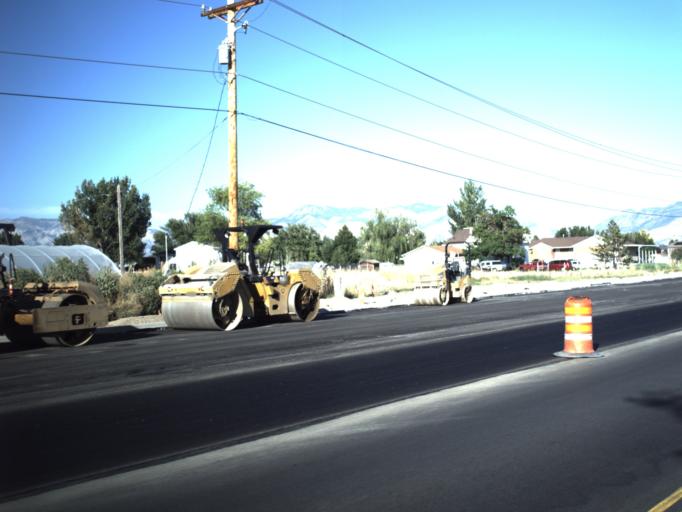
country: US
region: Utah
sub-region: Weber County
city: West Haven
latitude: 41.1907
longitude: -112.0745
